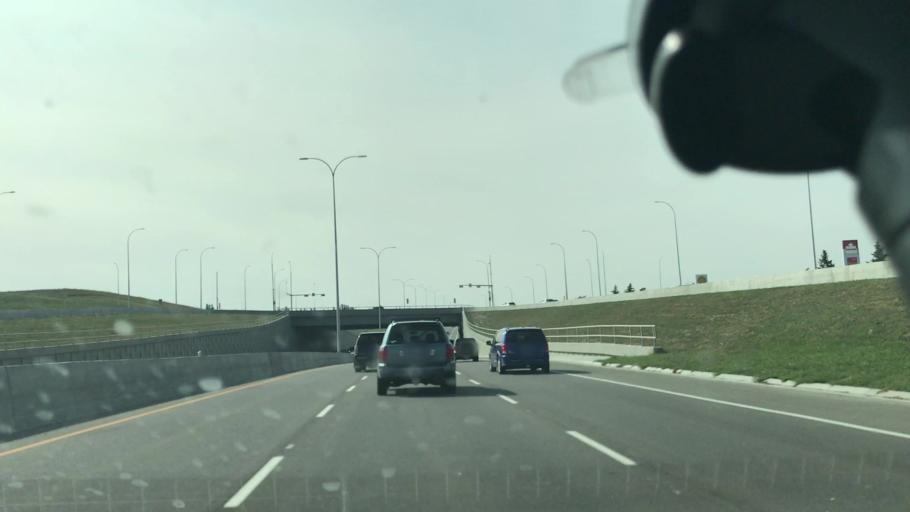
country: CA
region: Alberta
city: Calgary
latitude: 51.0836
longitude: -114.2059
